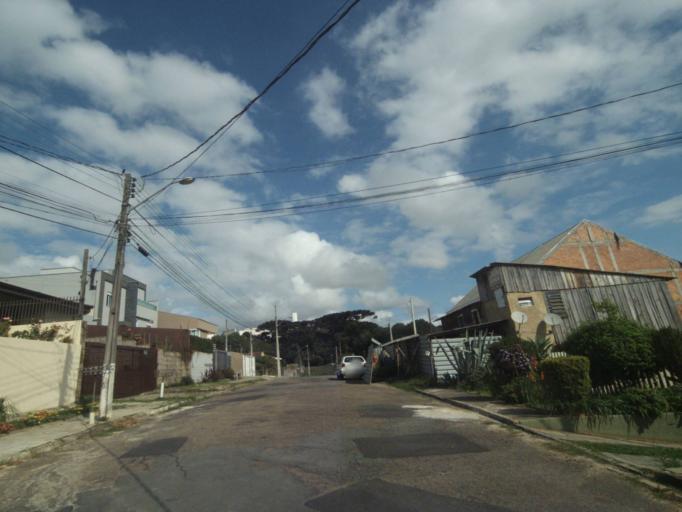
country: BR
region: Parana
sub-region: Curitiba
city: Curitiba
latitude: -25.3834
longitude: -49.2967
